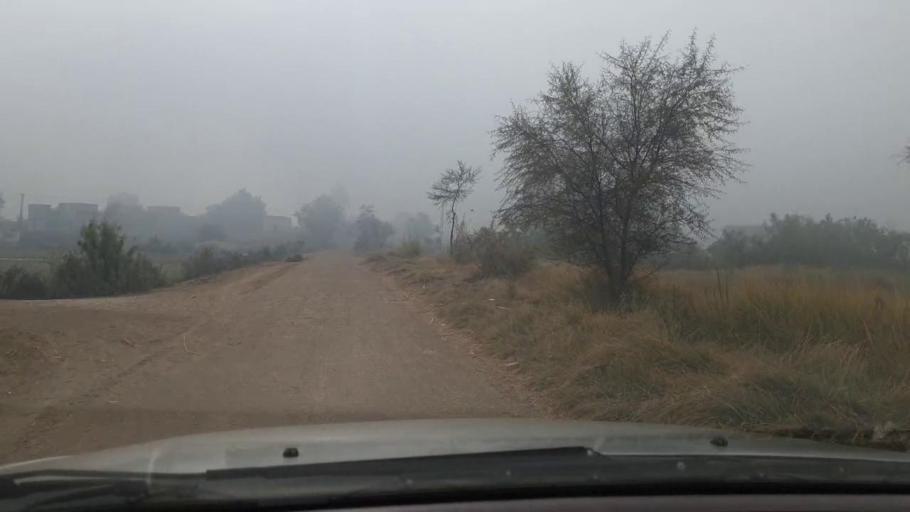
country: PK
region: Sindh
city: Khanpur
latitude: 27.8497
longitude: 69.4866
